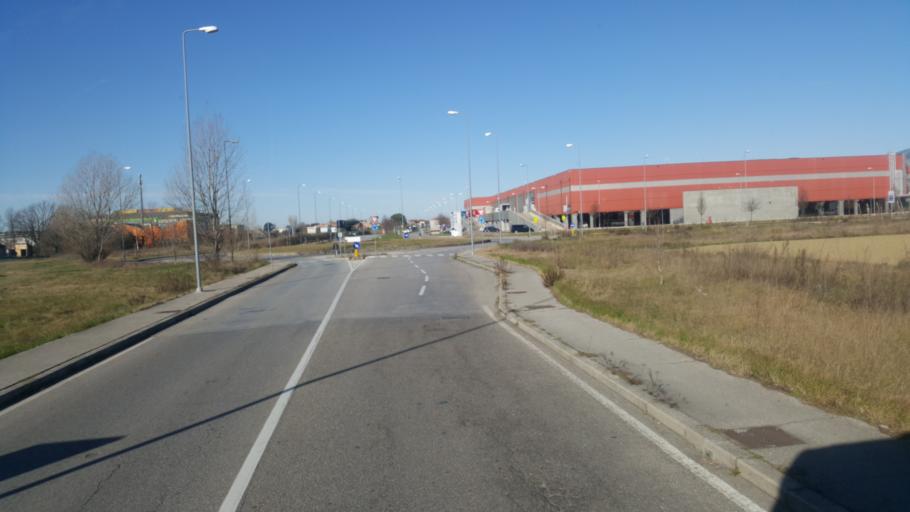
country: IT
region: Emilia-Romagna
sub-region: Forli-Cesena
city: Forli
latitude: 44.2417
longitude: 12.0844
